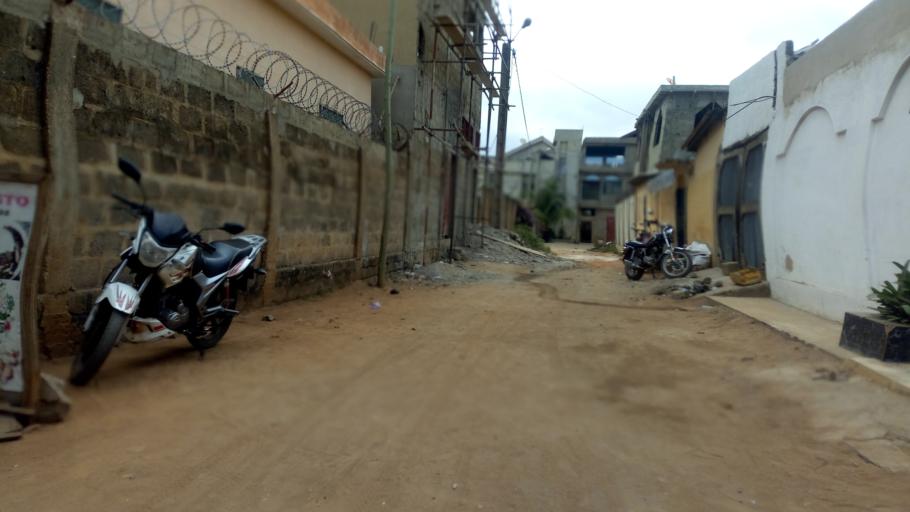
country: TG
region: Maritime
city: Lome
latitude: 6.2106
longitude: 1.1805
